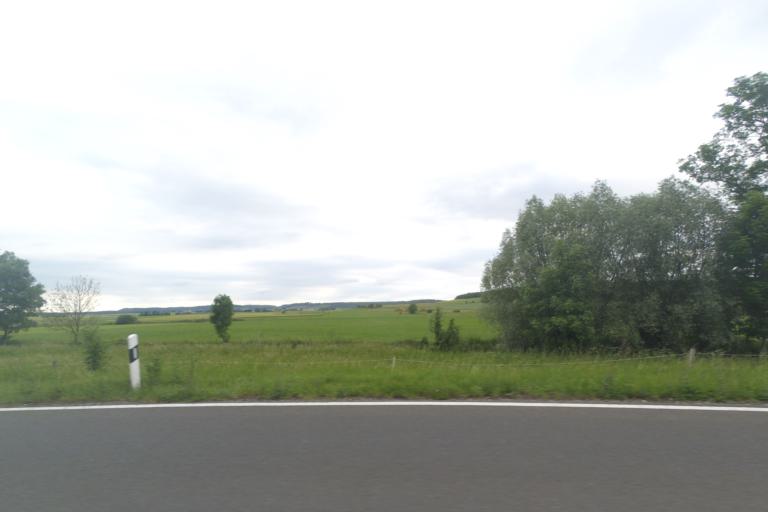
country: DE
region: Bavaria
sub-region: Regierungsbezirk Mittelfranken
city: Sugenheim
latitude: 49.6155
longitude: 10.4599
